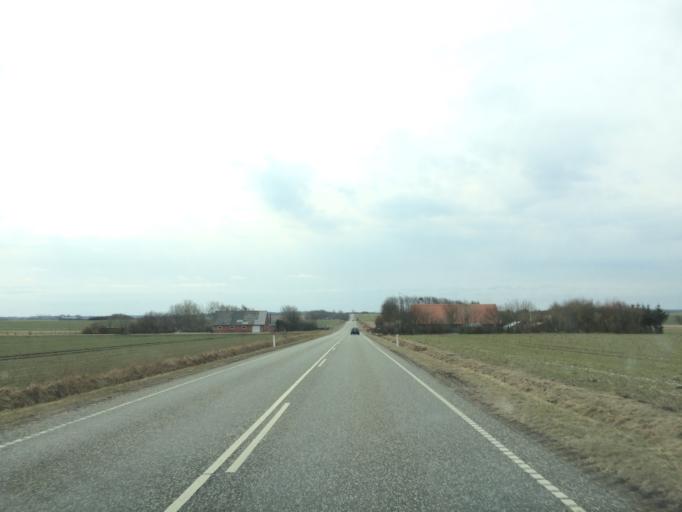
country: DK
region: Central Jutland
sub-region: Ringkobing-Skjern Kommune
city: Skjern
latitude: 56.0474
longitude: 8.5040
